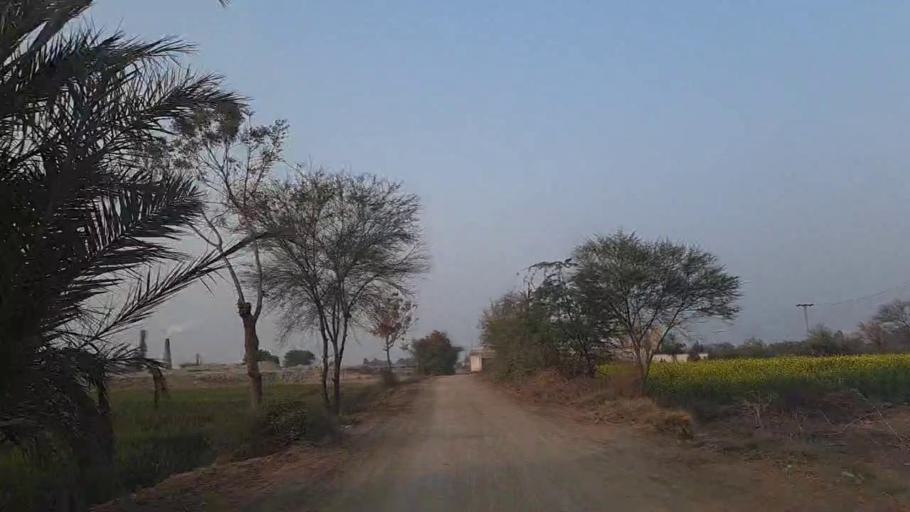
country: PK
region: Sindh
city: Nawabshah
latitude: 26.2802
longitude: 68.4648
